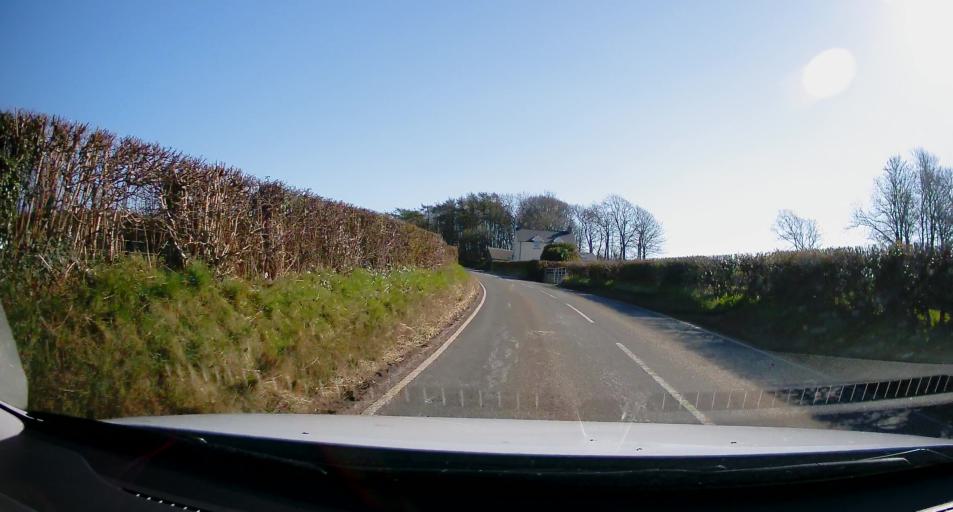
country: GB
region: Wales
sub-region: County of Ceredigion
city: Penparcau
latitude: 52.3563
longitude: -4.0576
